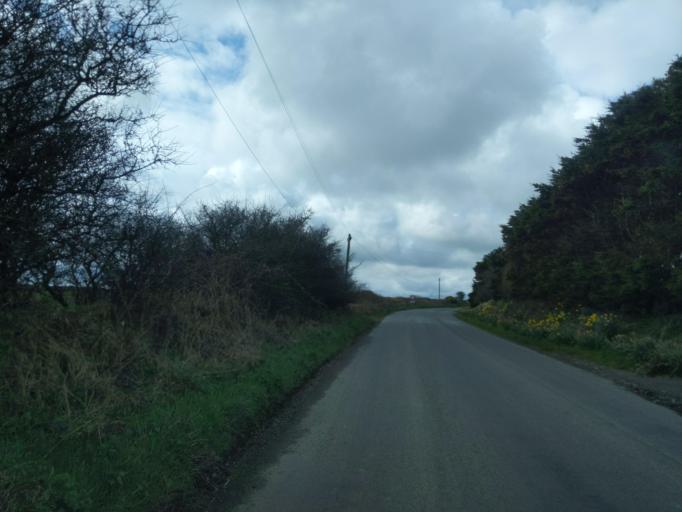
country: GB
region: England
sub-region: Cornwall
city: Camelford
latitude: 50.6409
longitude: -4.6486
